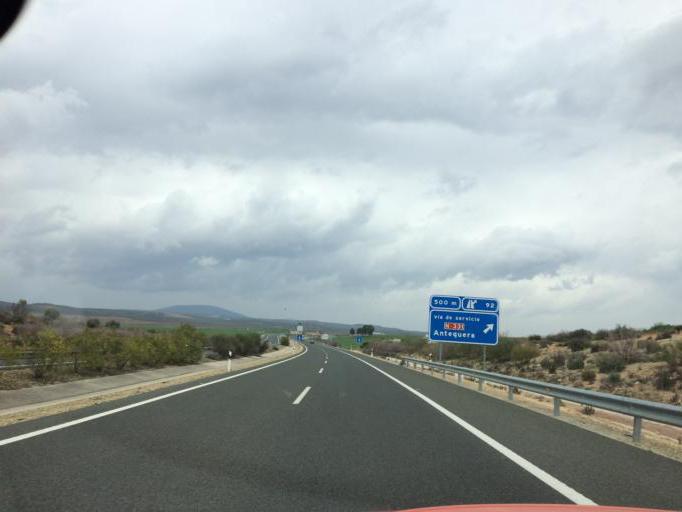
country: ES
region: Andalusia
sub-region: Provincia de Malaga
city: Antequera
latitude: 37.1036
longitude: -4.5564
